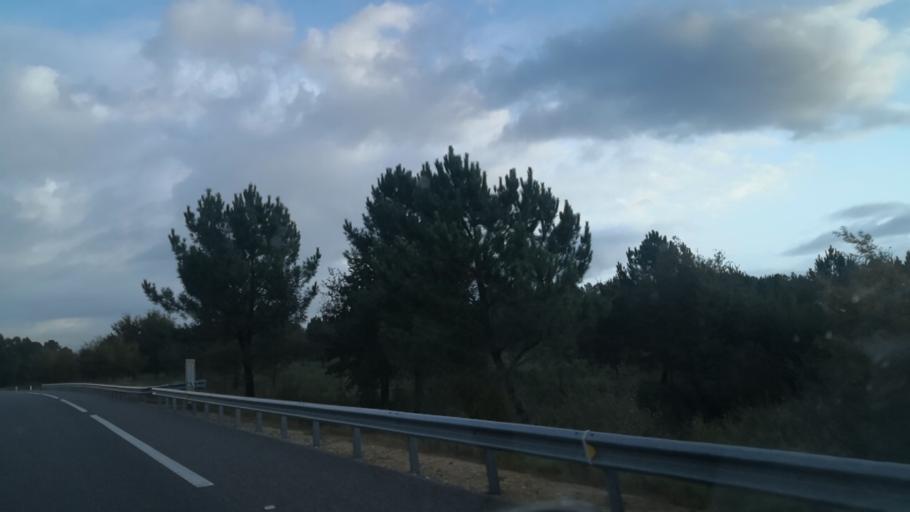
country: ES
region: Galicia
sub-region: Provincia de Pontevedra
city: Porrino
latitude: 42.1236
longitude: -8.6396
